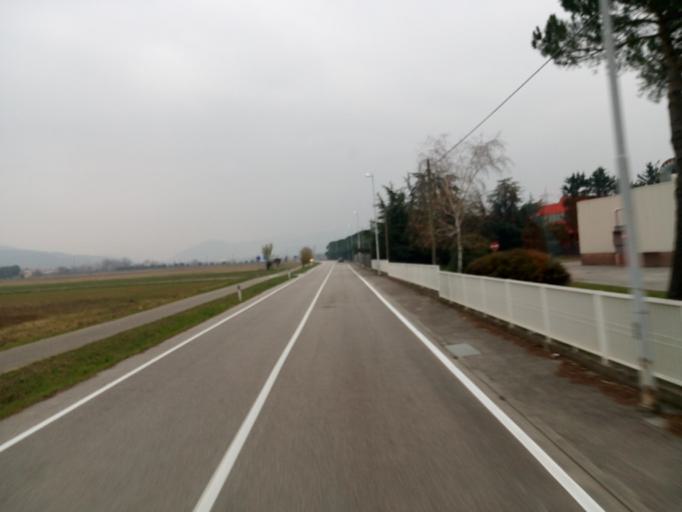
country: IT
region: Friuli Venezia Giulia
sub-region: Provincia di Udine
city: Moimacco
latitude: 46.0921
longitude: 13.3937
